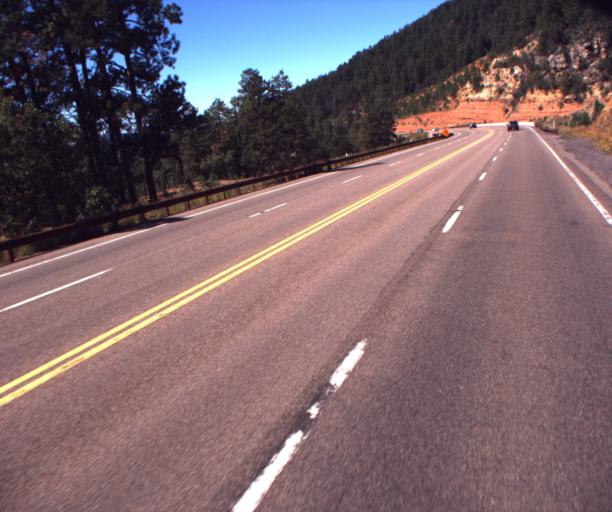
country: US
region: Arizona
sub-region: Gila County
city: Star Valley
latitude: 34.3062
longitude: -110.9285
